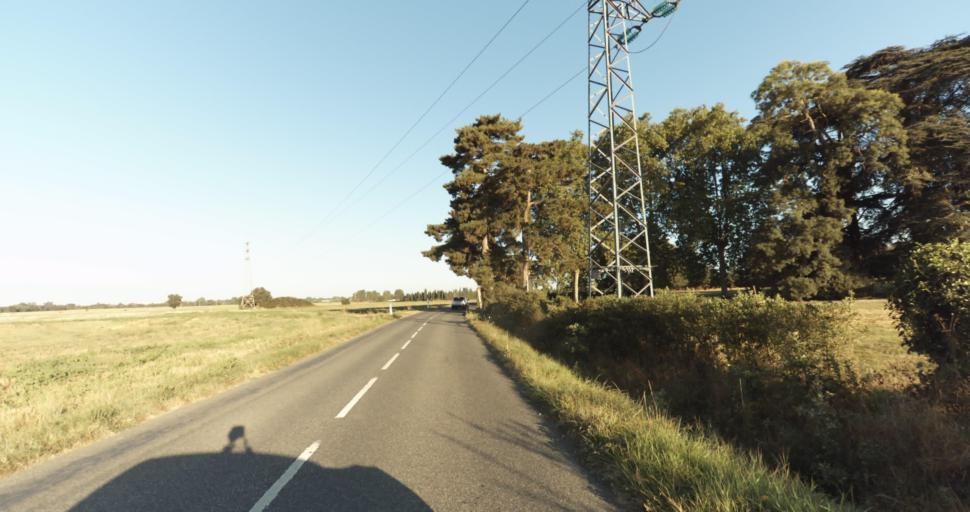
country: FR
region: Midi-Pyrenees
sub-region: Departement de la Haute-Garonne
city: L'Union
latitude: 43.6666
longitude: 1.4678
